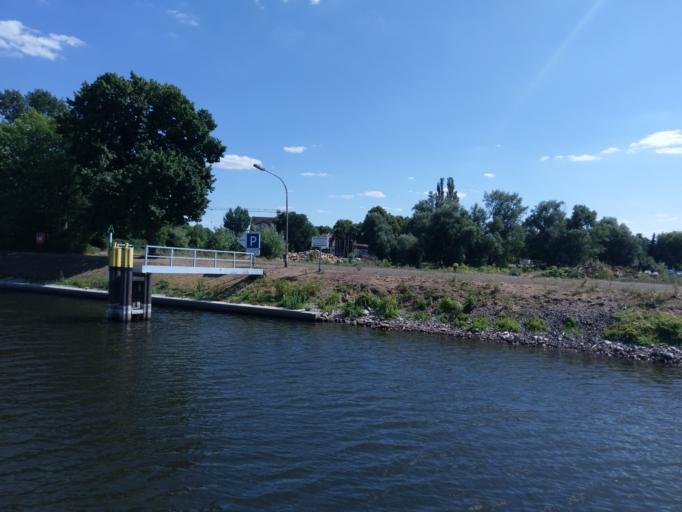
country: DE
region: Brandenburg
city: Brandenburg an der Havel
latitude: 52.4225
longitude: 12.5690
